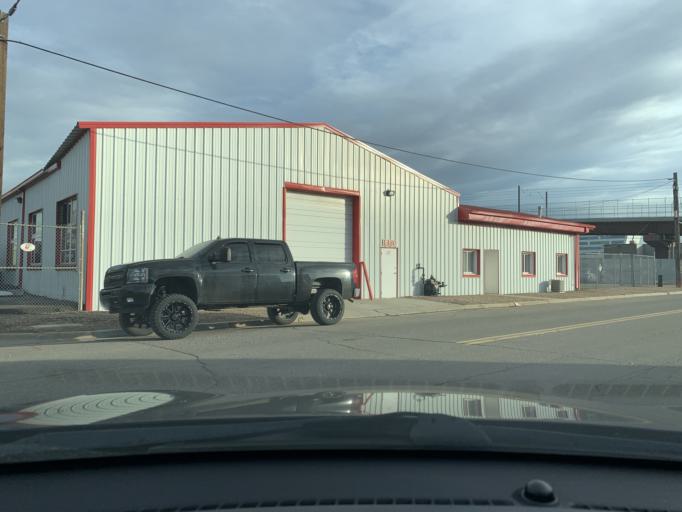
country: US
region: Colorado
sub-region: Denver County
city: Denver
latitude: 39.7385
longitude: -105.0124
